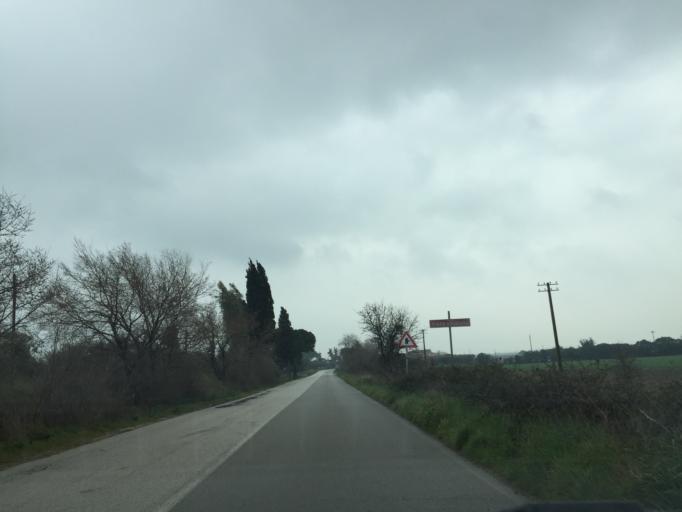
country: IT
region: Apulia
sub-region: Provincia di Foggia
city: Foggia
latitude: 41.4145
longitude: 15.4557
